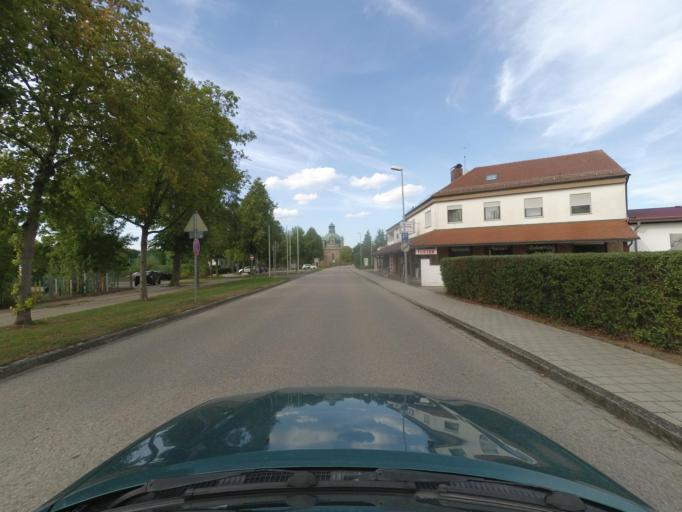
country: DE
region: Bavaria
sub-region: Upper Palatinate
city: Freystadt
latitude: 49.2016
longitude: 11.3266
